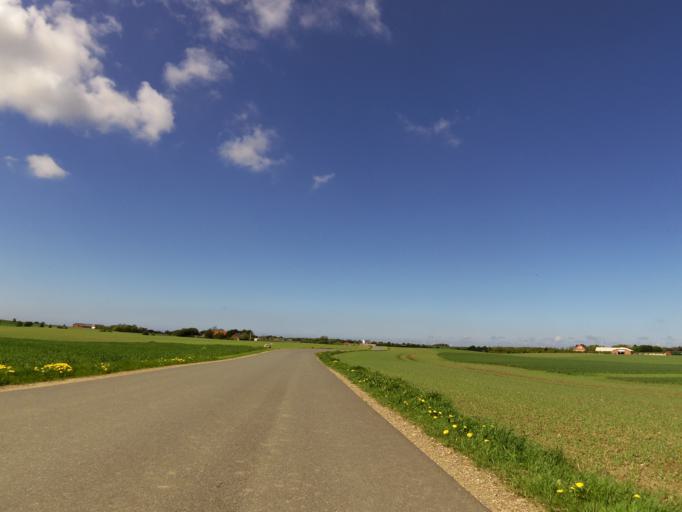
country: DK
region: Central Jutland
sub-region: Holstebro Kommune
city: Vinderup
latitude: 56.4184
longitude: 8.7861
